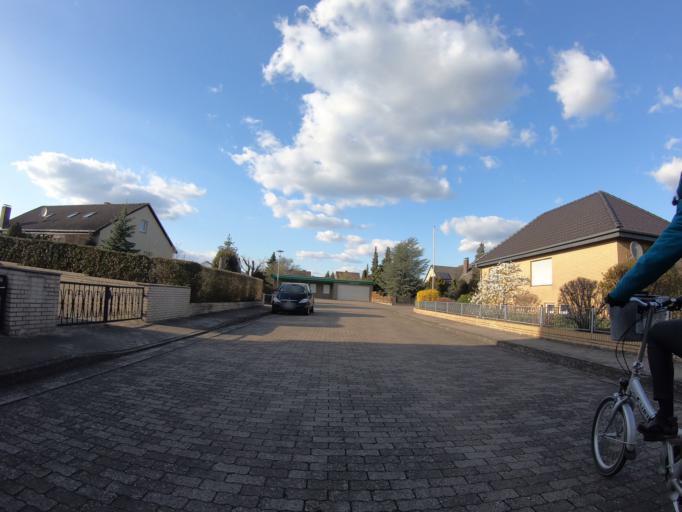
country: DE
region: Lower Saxony
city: Wesendorf
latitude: 52.5922
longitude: 10.5396
